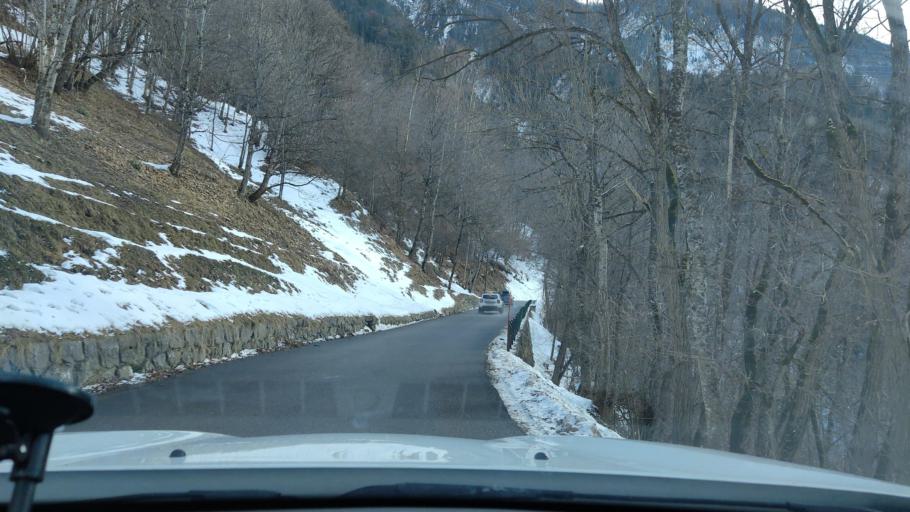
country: FR
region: Rhone-Alpes
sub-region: Departement de la Savoie
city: Salins-les-Thermes
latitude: 45.4321
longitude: 6.5010
